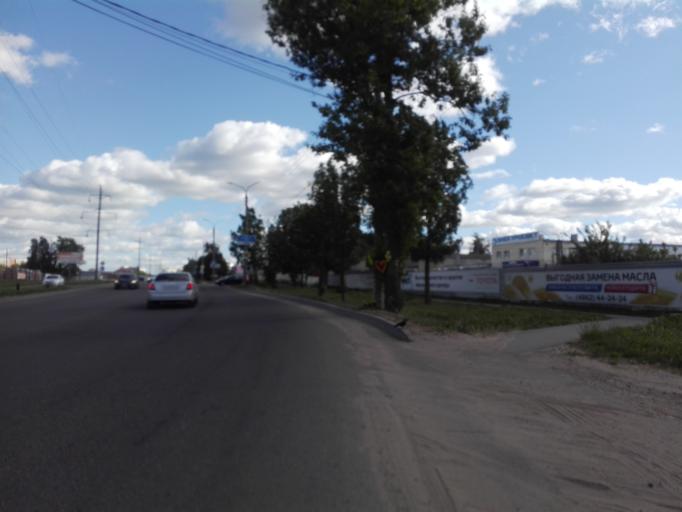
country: RU
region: Orjol
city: Orel
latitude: 52.9457
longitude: 36.0317
